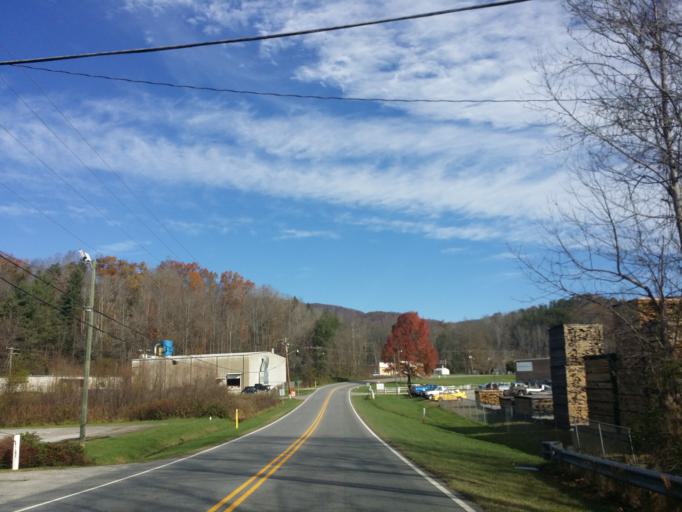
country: US
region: North Carolina
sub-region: McDowell County
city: West Marion
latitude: 35.6342
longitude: -82.1721
